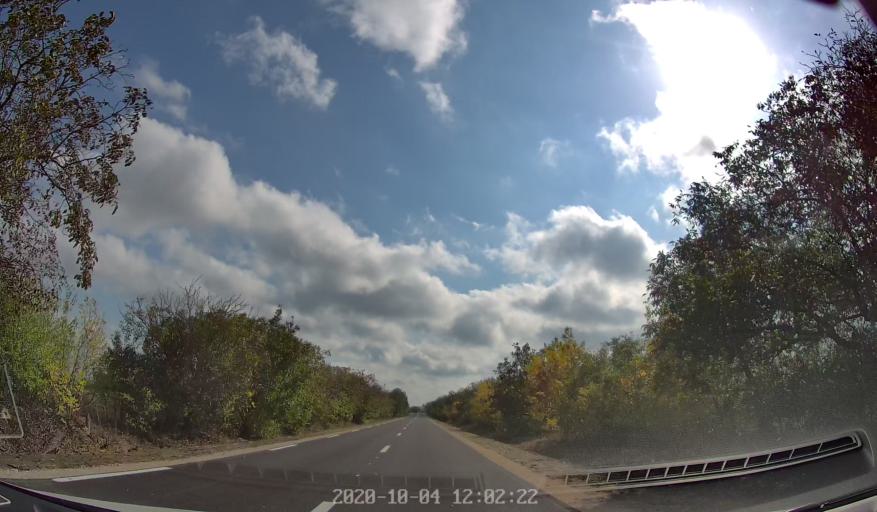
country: MD
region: Rezina
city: Saharna
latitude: 47.6175
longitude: 28.9058
